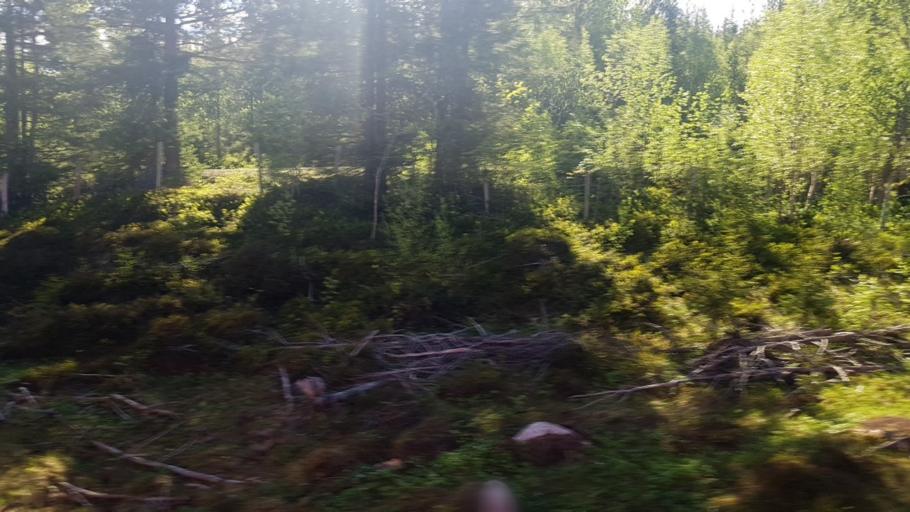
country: NO
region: Sor-Trondelag
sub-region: Rennebu
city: Berkak
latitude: 62.8325
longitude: 10.0165
